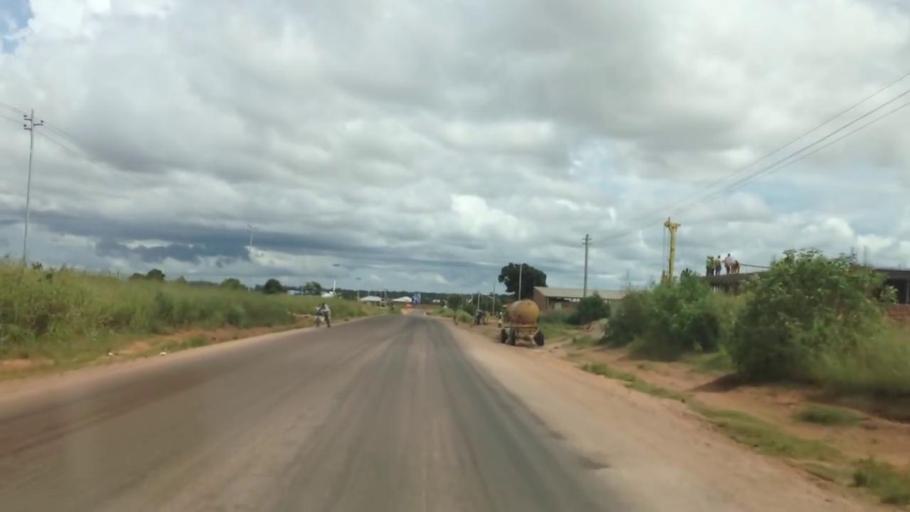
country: CD
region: Katanga
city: Kolwezi
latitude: -10.7486
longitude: 25.5155
